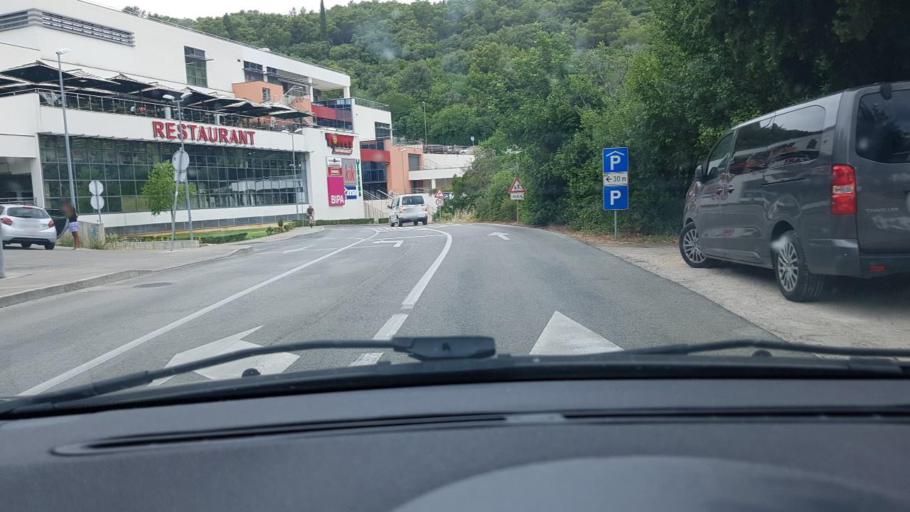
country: HR
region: Dubrovacko-Neretvanska
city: Korcula
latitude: 42.9571
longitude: 17.1337
